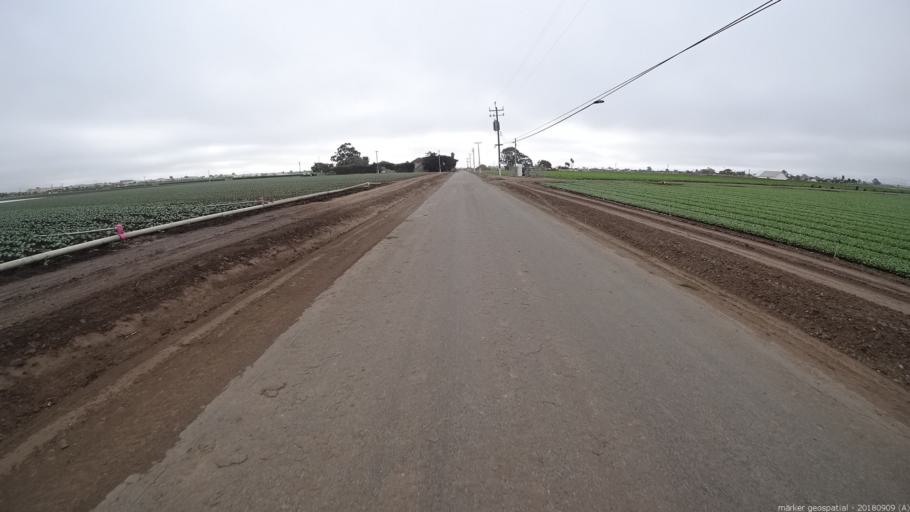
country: US
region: California
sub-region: Monterey County
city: Boronda
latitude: 36.7155
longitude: -121.6784
